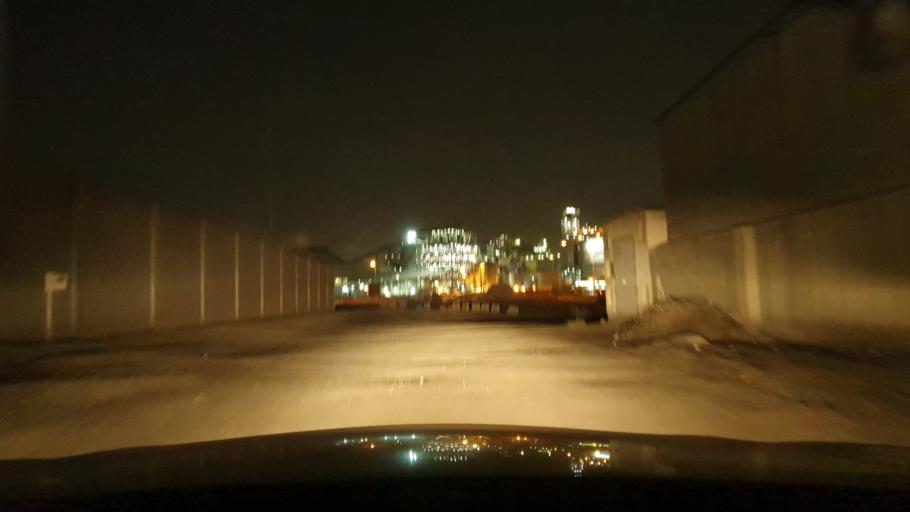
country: BH
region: Northern
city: Sitrah
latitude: 26.0954
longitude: 50.6105
